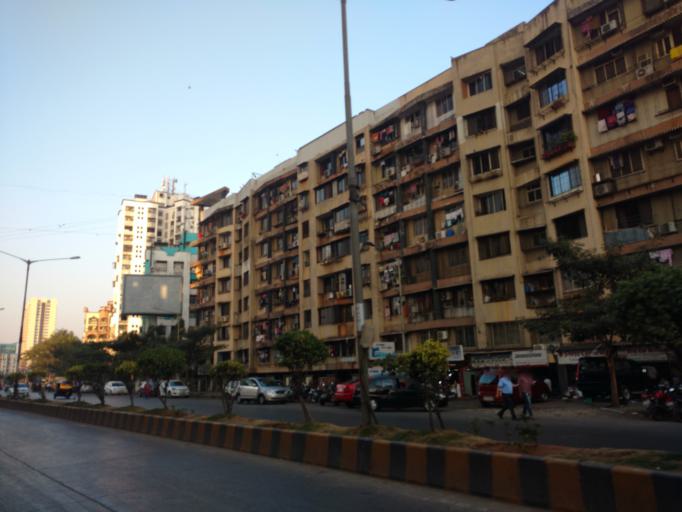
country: IN
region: Maharashtra
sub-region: Mumbai Suburban
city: Borivli
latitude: 19.2117
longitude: 72.8358
